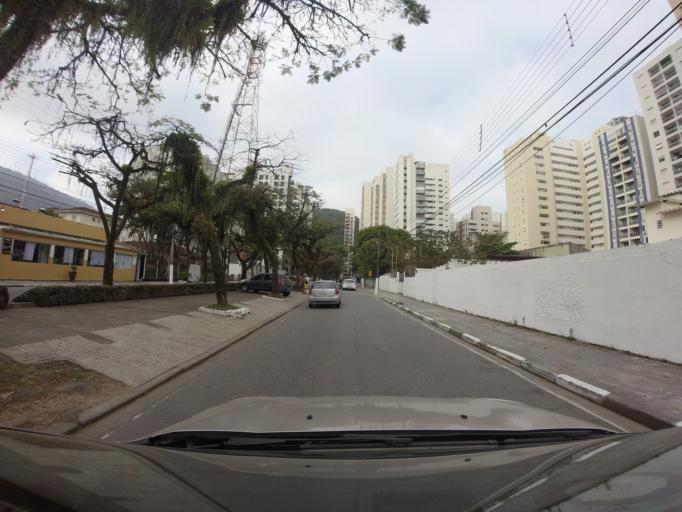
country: BR
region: Sao Paulo
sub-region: Guaruja
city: Guaruja
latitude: -23.9942
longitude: -46.2557
